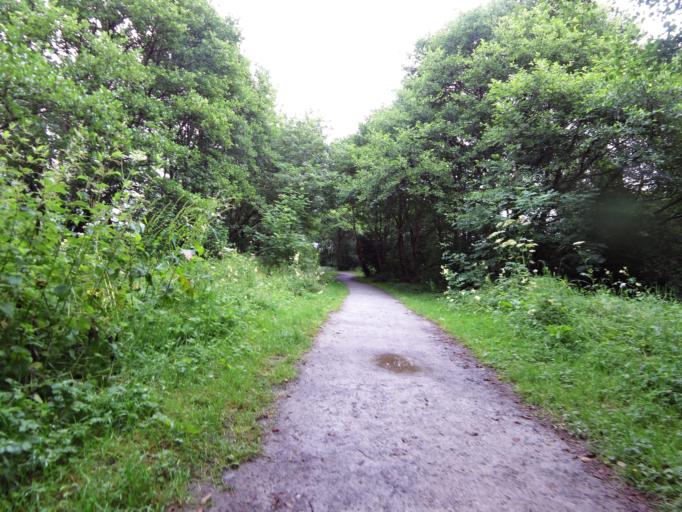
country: GB
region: Scotland
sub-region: Highland
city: Fort William
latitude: 56.8277
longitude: -5.0955
